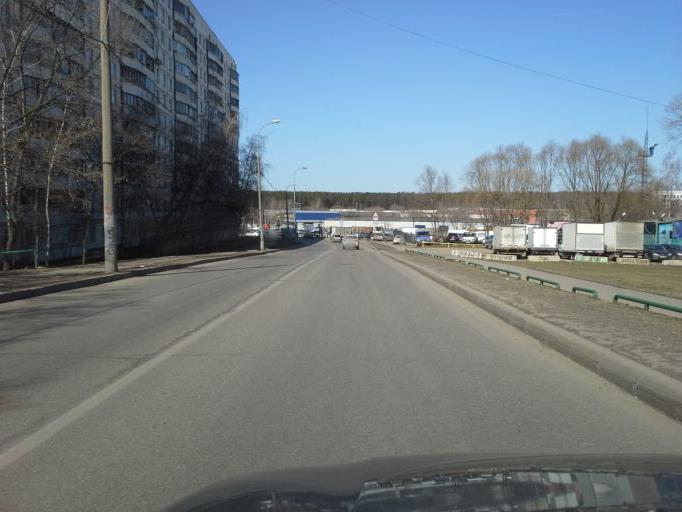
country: RU
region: Moscow
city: Mikhalkovo
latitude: 55.6572
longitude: 37.4130
